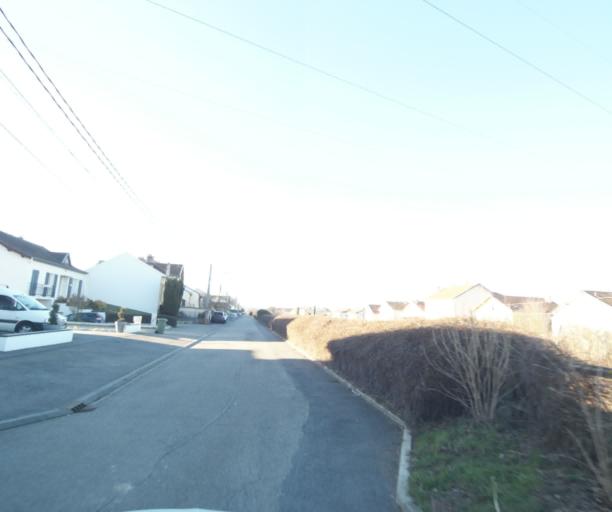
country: FR
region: Lorraine
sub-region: Departement de Meurthe-et-Moselle
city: Laneuveville-devant-Nancy
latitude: 48.6495
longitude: 6.2376
